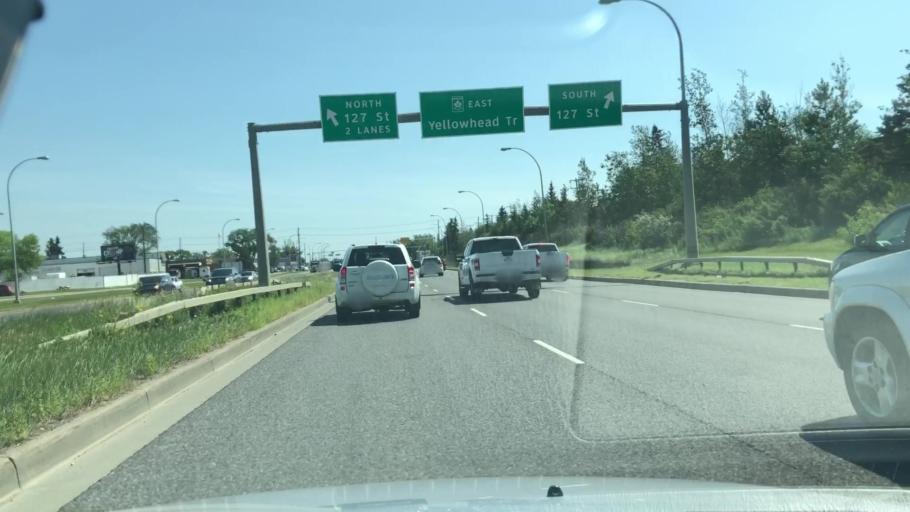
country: CA
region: Alberta
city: Edmonton
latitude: 53.5808
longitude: -113.5464
